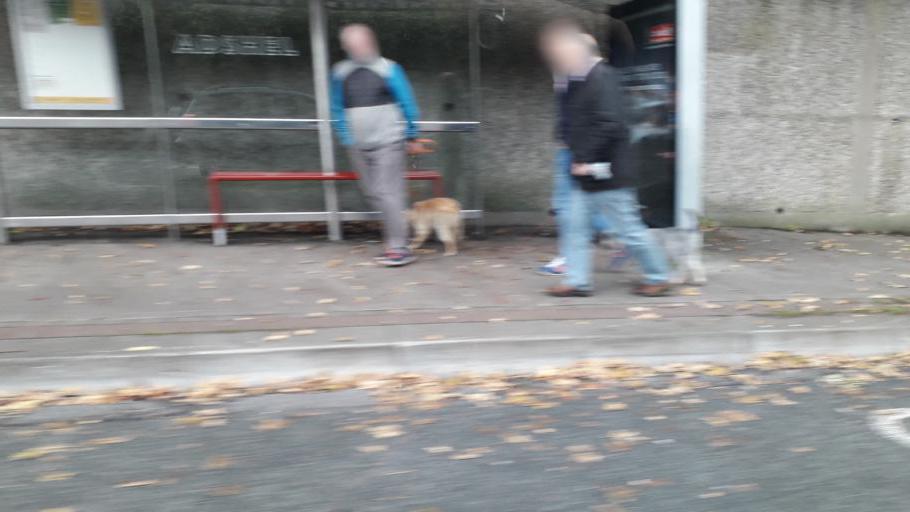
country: IE
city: Milltown
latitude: 53.3123
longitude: -6.2388
